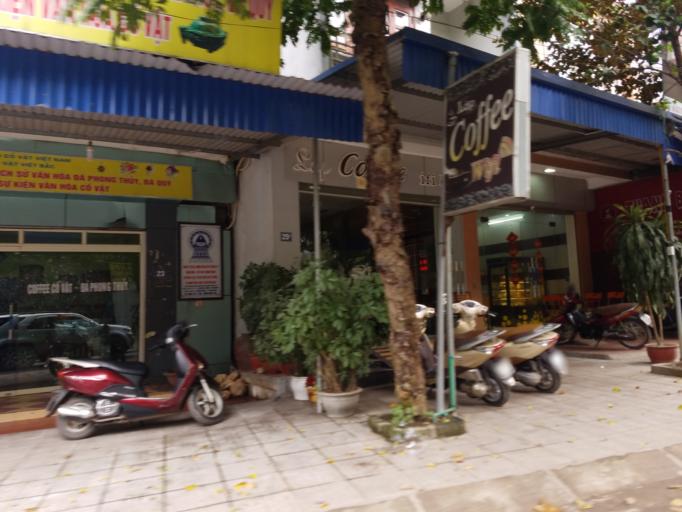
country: VN
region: Thai Nguyen
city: Thanh Pho Thai Nguyen
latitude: 21.5928
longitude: 105.8433
